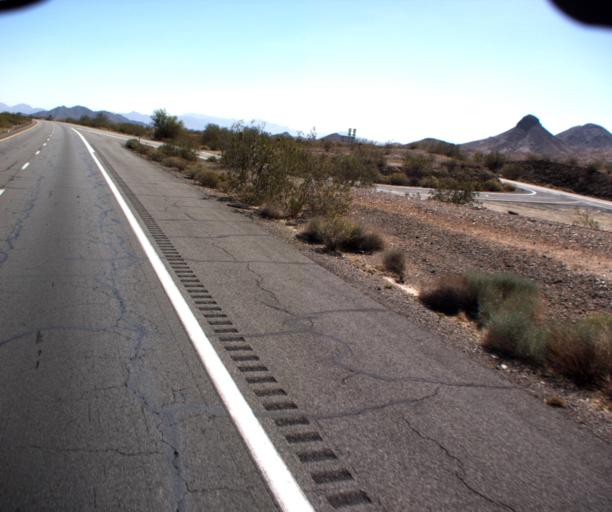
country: US
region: Arizona
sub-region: La Paz County
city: Quartzsite
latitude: 33.6466
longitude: -114.3346
